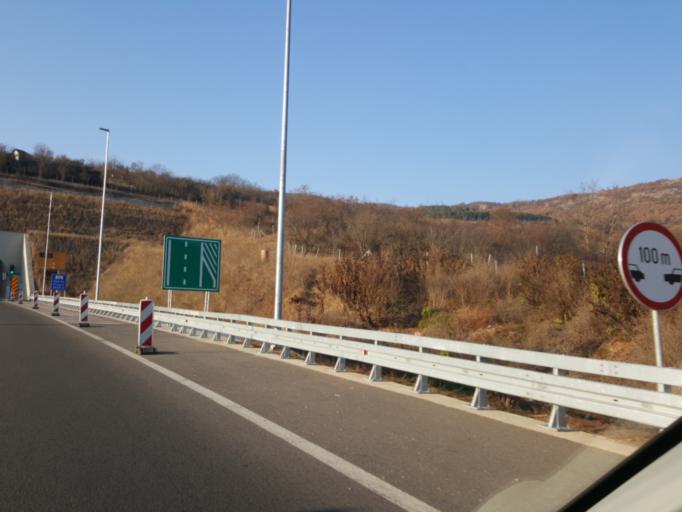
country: RS
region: Central Serbia
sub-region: Pirotski Okrug
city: Dimitrovgrad
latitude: 43.0231
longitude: 22.7945
